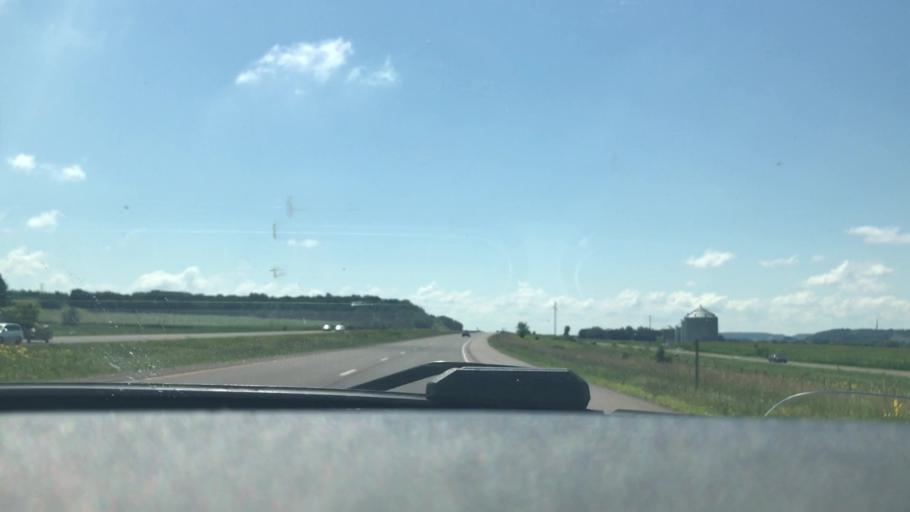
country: US
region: Wisconsin
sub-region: Chippewa County
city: Bloomer
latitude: 45.0354
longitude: -91.4541
